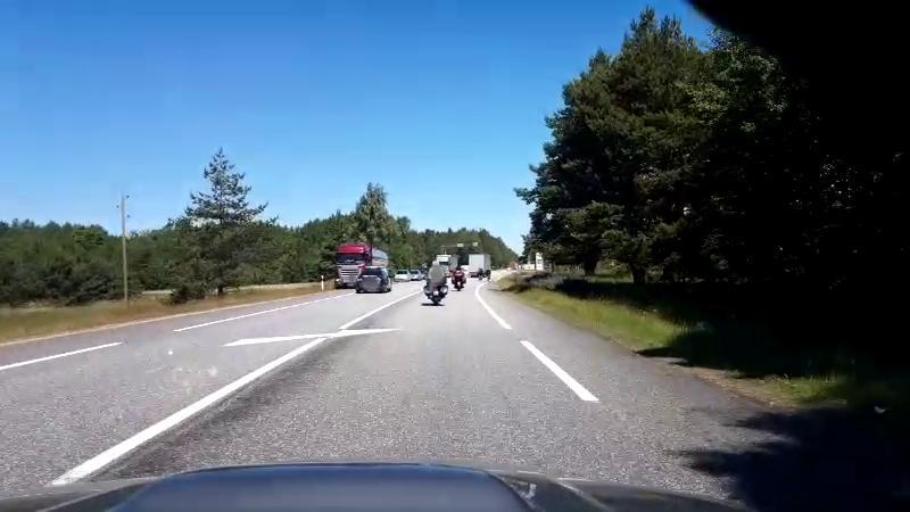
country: LV
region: Saulkrastu
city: Saulkrasti
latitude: 57.3866
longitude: 24.4292
